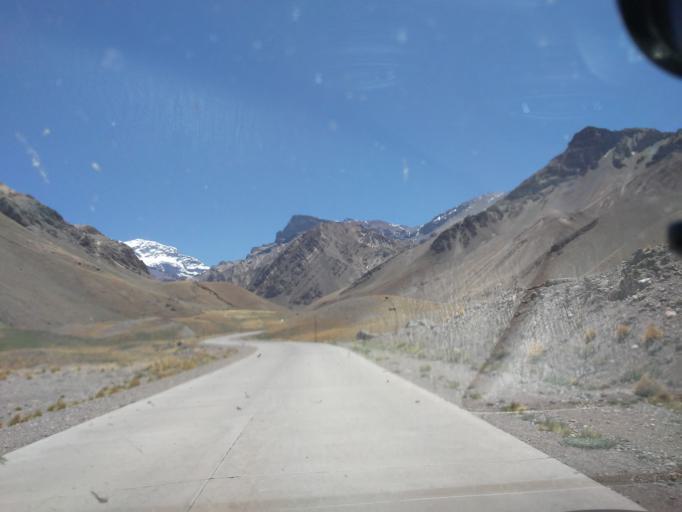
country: CL
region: Valparaiso
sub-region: Provincia de Los Andes
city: Los Andes
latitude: -32.8183
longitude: -69.9423
